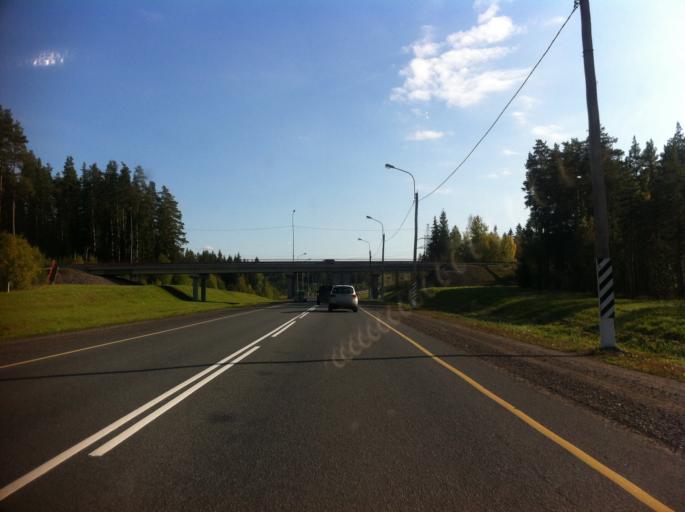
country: RU
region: Leningrad
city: Luga
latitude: 58.7588
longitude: 29.8862
